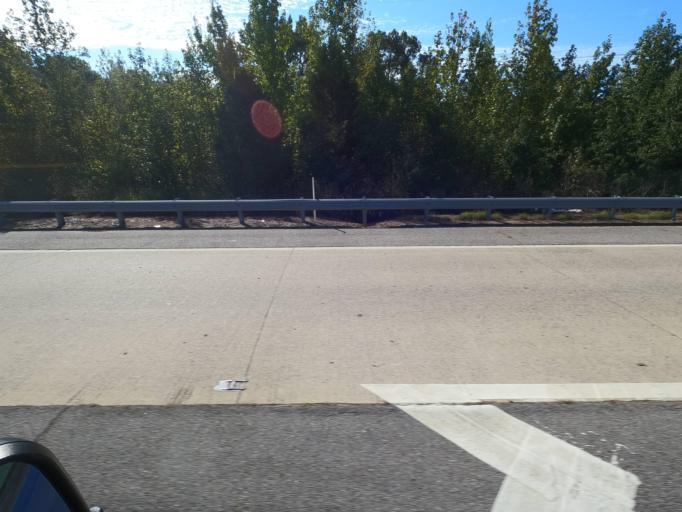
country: US
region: Tennessee
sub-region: Shelby County
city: Arlington
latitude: 35.3115
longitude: -89.7258
